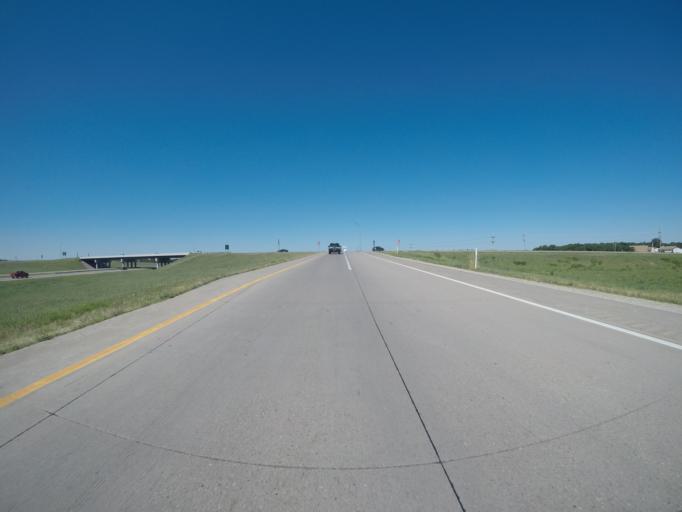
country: US
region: Kansas
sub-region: Saline County
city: Salina
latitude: 38.8833
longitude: -97.5930
